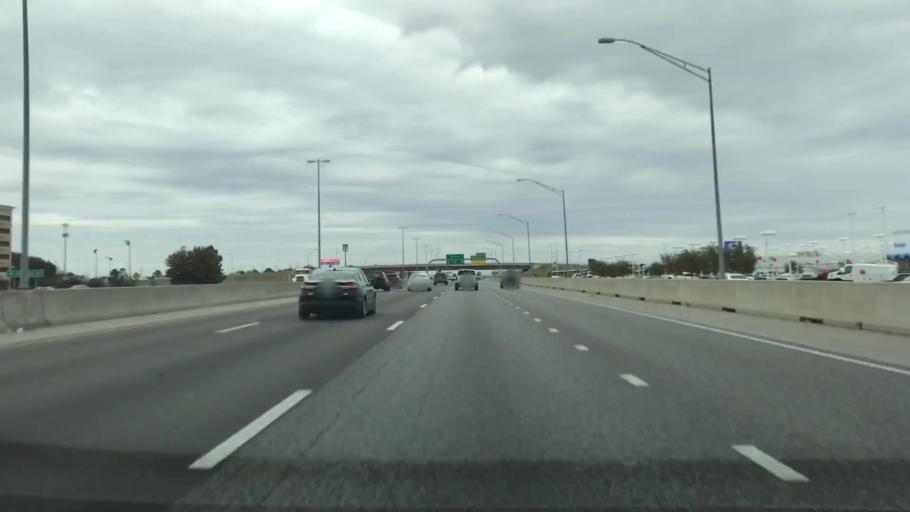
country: US
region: Oklahoma
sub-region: Cleveland County
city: Norman
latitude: 35.2290
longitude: -97.4854
